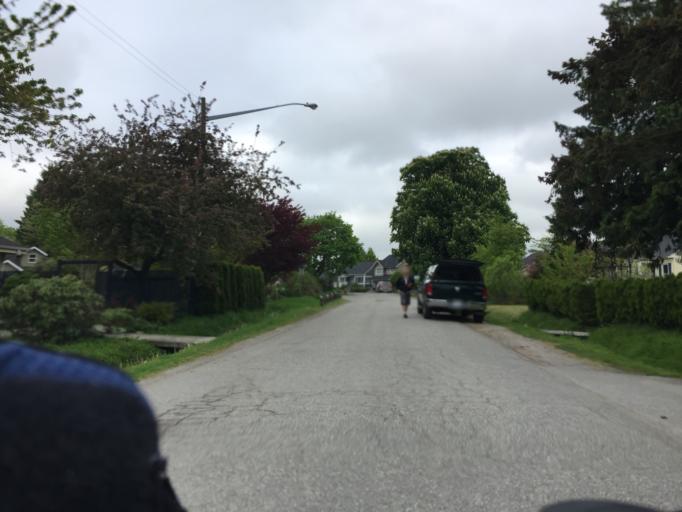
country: CA
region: British Columbia
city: Richmond
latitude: 49.1912
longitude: -123.1467
